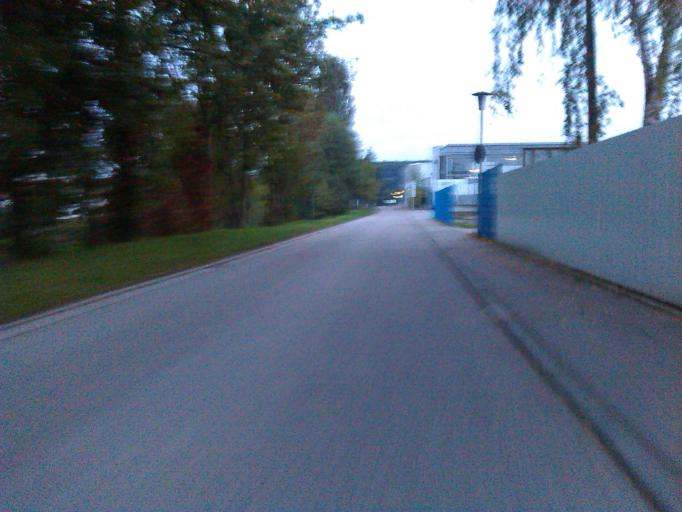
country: DE
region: Baden-Wuerttemberg
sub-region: Karlsruhe Region
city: Zuzenhausen
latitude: 49.2702
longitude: 8.8392
